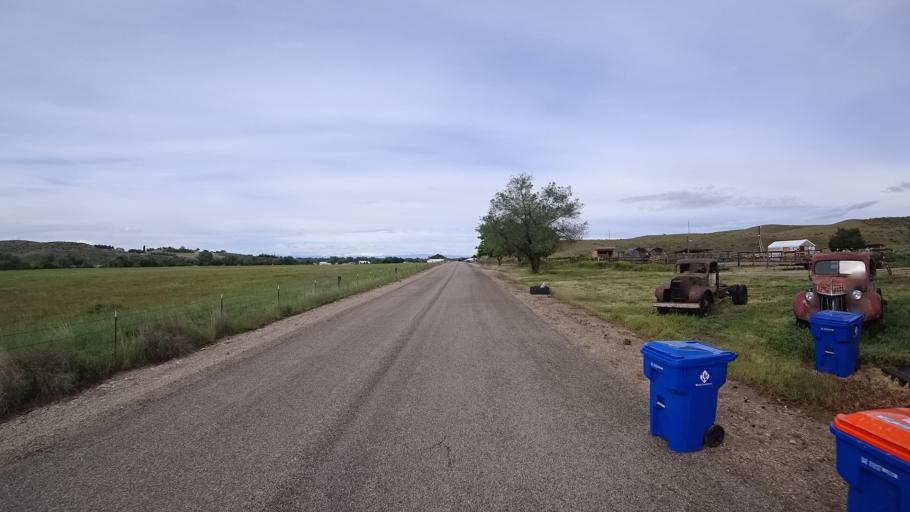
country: US
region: Idaho
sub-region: Ada County
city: Eagle
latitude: 43.7345
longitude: -116.3105
